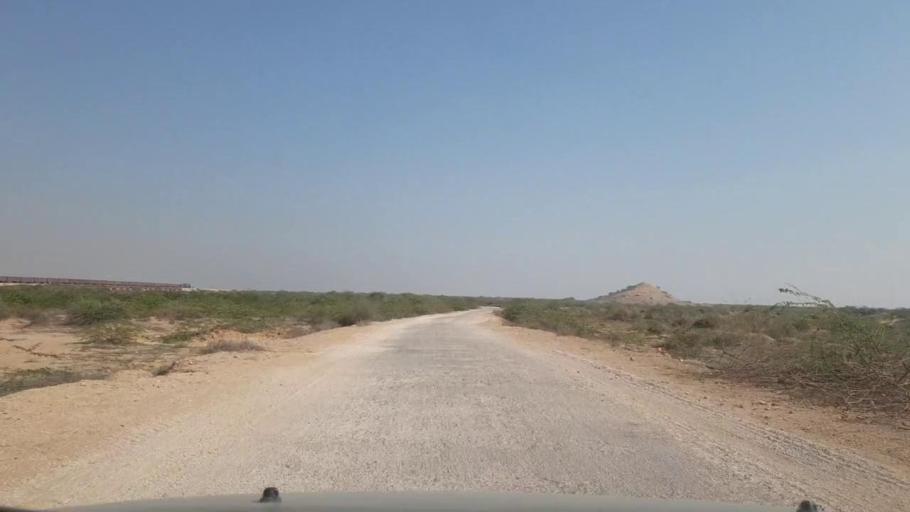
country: PK
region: Sindh
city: Thatta
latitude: 24.9795
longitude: 67.9843
